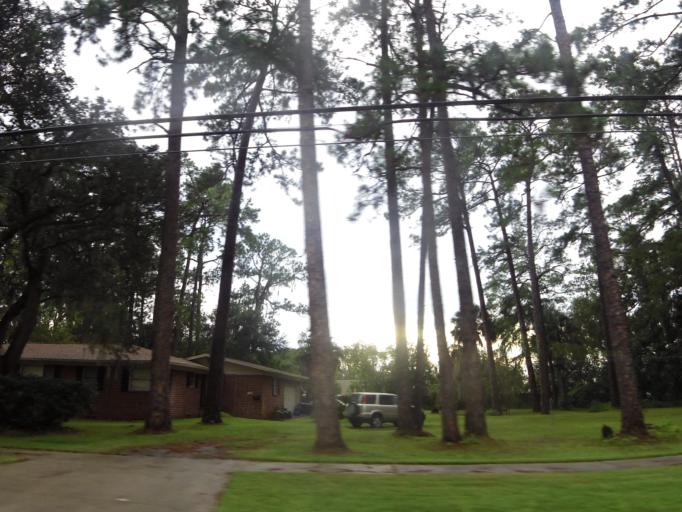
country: US
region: Florida
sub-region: Duval County
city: Jacksonville
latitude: 30.2893
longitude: -81.5959
